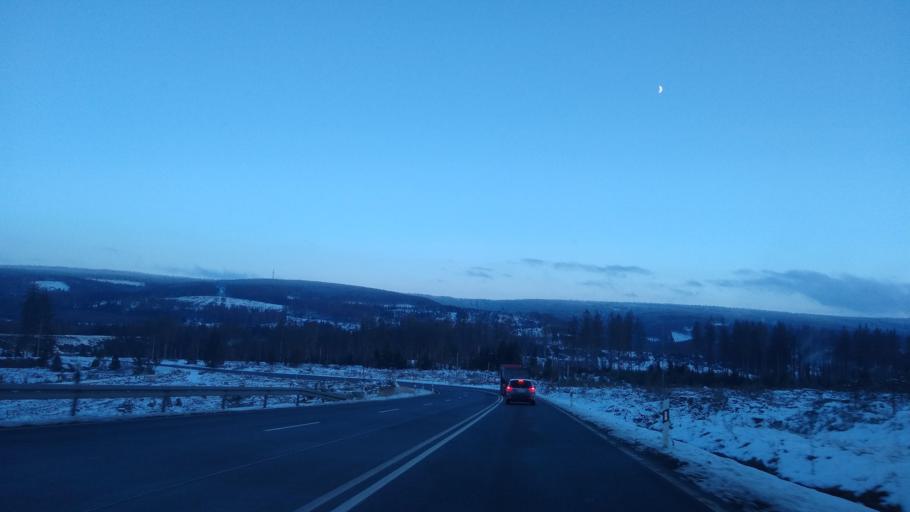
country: DE
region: Lower Saxony
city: Altenau
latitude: 51.7823
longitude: 10.4080
